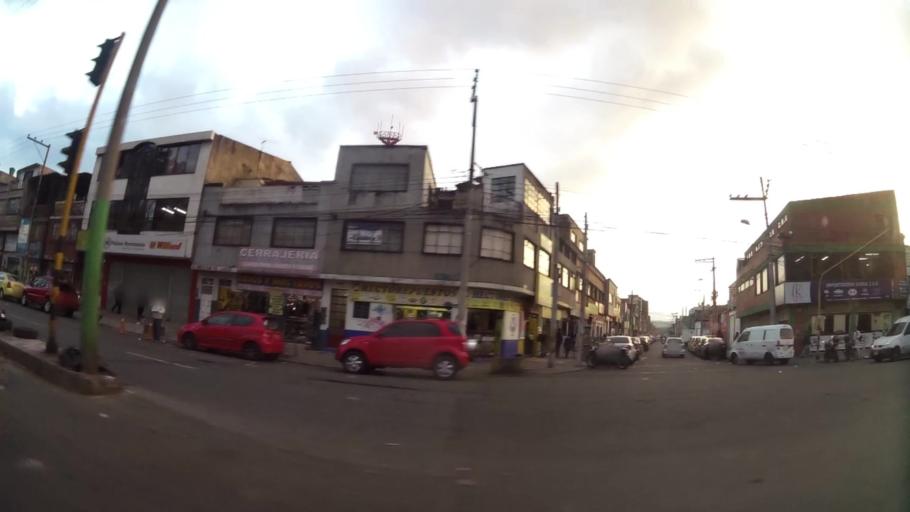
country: CO
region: Bogota D.C.
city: Bogota
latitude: 4.5935
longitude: -74.0944
